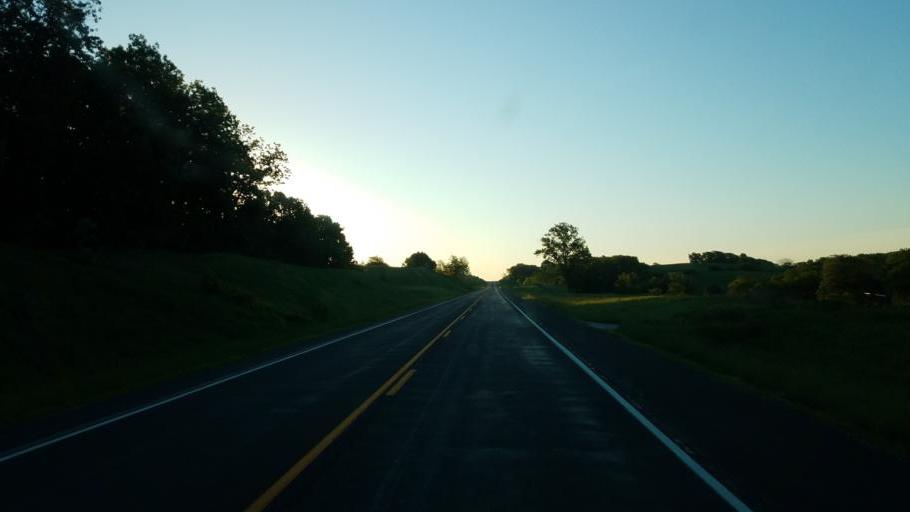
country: US
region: Missouri
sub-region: Schuyler County
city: Lancaster
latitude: 40.4925
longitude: -92.6006
